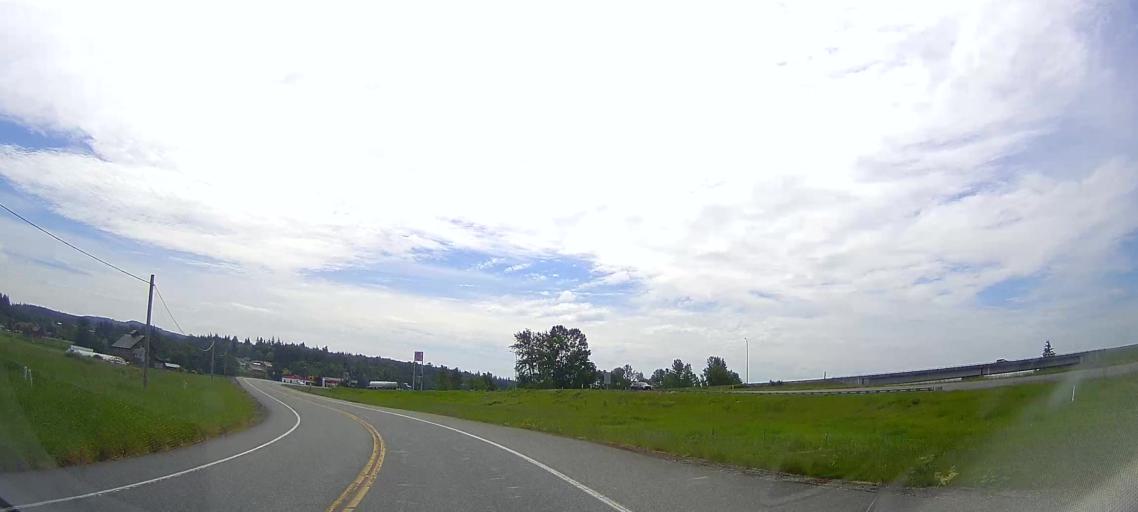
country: US
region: Washington
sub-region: Skagit County
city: Mount Vernon
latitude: 48.3429
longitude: -122.3341
